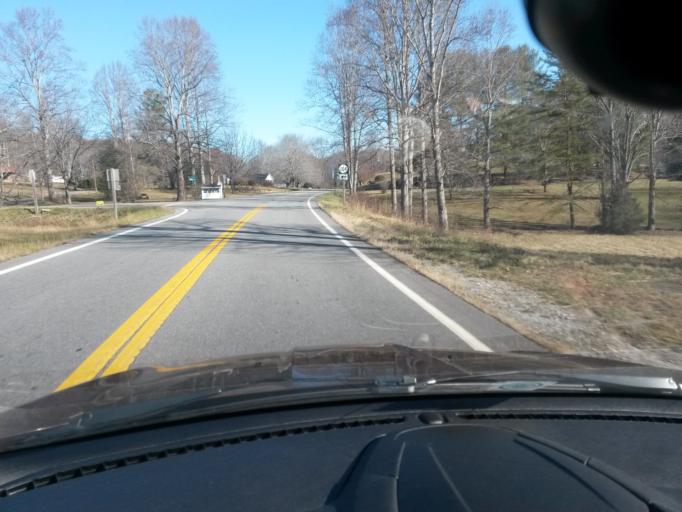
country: US
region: Virginia
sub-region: Henry County
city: Pannill Fork
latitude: 36.7802
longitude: -80.1330
